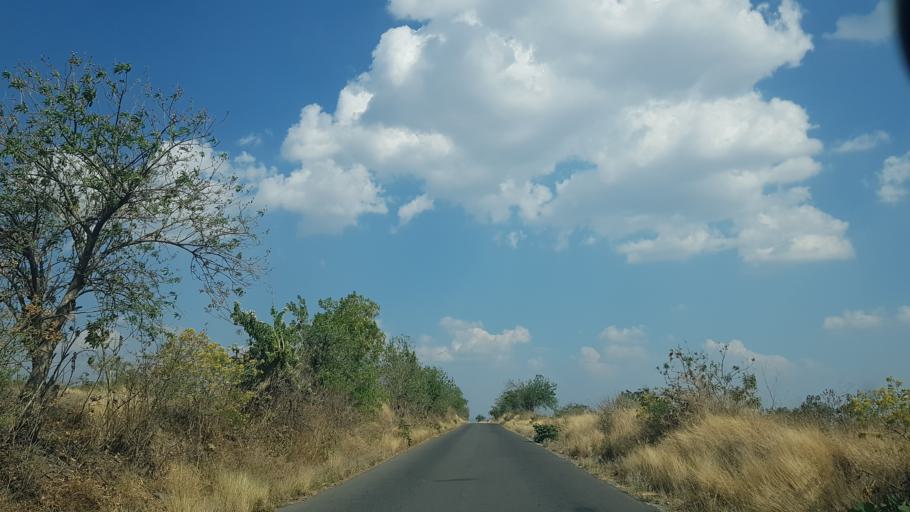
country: MX
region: Puebla
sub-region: Atlixco
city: Colonia Agricola de Ocotepec (Colonia San Jose)
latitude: 18.9203
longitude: -98.5323
